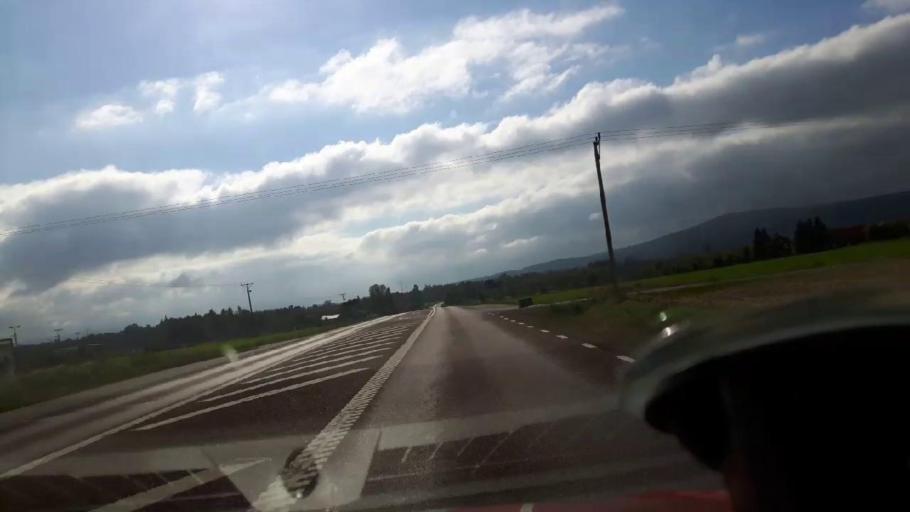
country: SE
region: Gaevleborg
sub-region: Bollnas Kommun
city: Arbra
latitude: 61.5310
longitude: 16.3634
